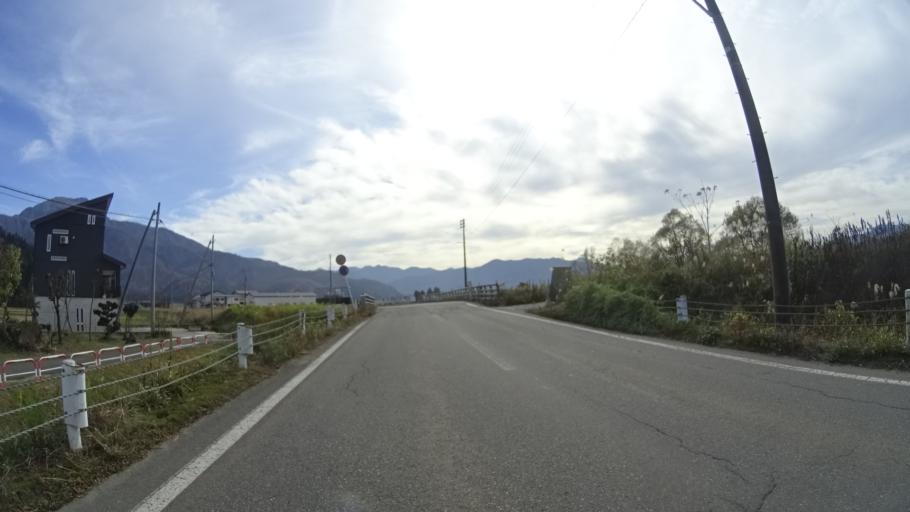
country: JP
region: Niigata
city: Muikamachi
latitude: 37.0492
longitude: 138.8807
